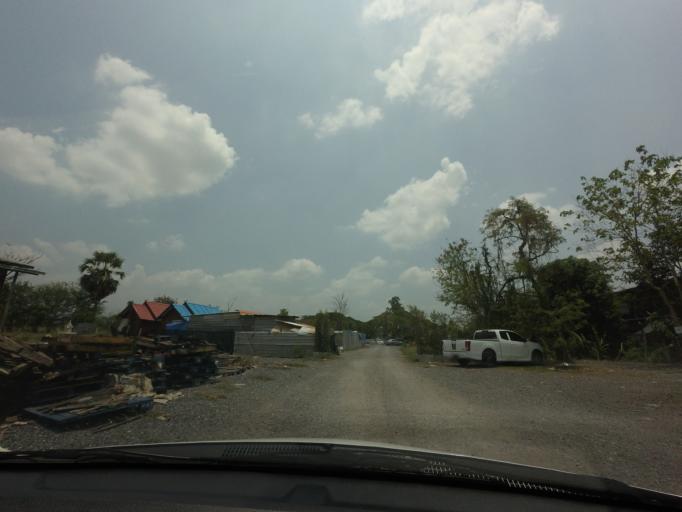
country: TH
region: Pathum Thani
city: Sam Khok
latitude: 14.0455
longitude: 100.5512
